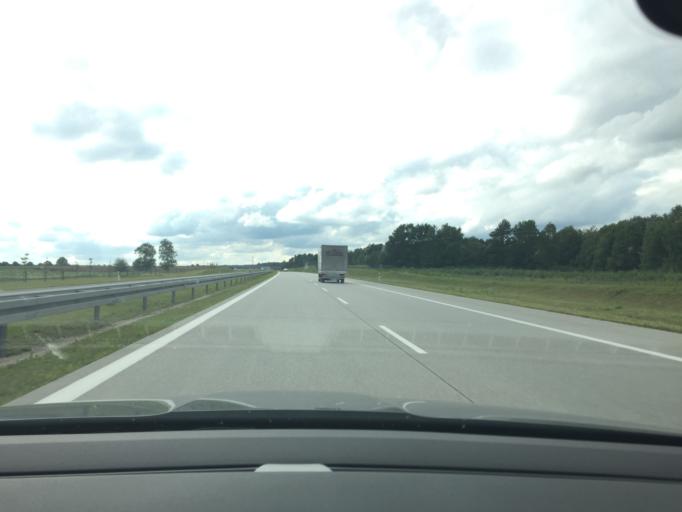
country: PL
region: Lubusz
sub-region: Powiat sulecinski
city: Torzym
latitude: 52.3203
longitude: 15.1894
